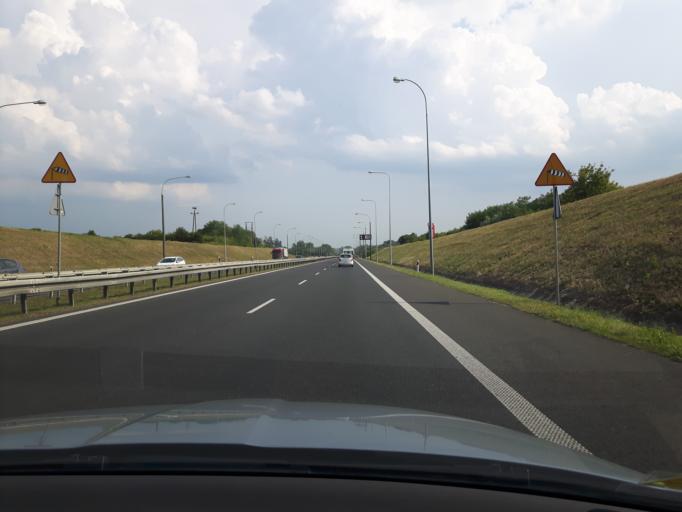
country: PL
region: Masovian Voivodeship
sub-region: Powiat nowodworski
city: Zakroczym
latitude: 52.4322
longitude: 20.6515
